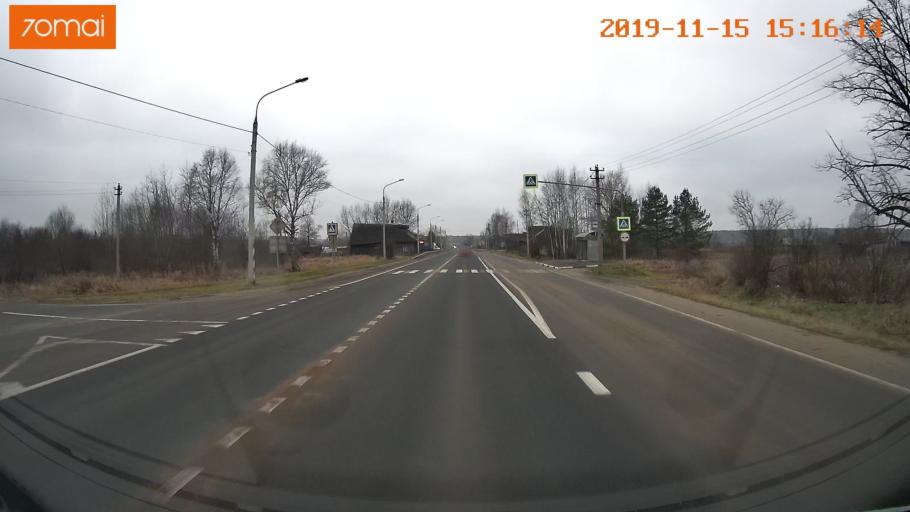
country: RU
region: Jaroslavl
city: Danilov
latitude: 58.2746
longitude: 40.1929
